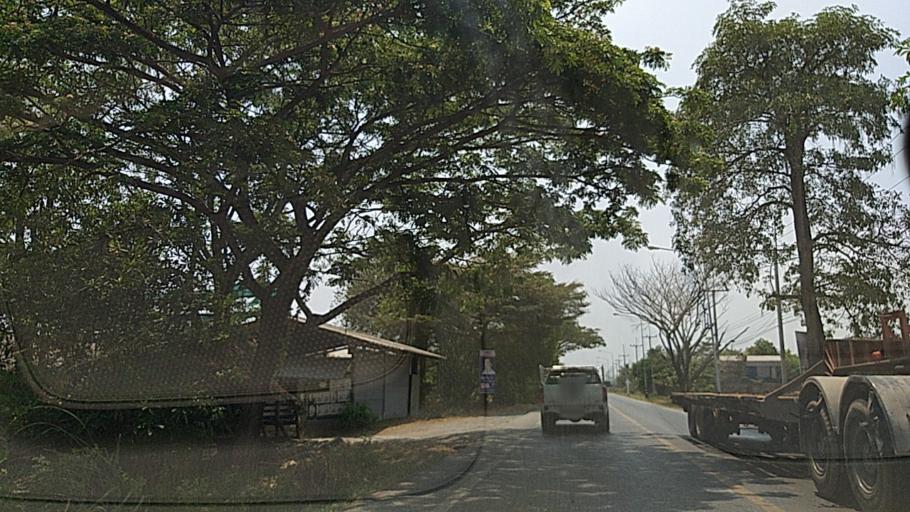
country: TH
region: Chachoengsao
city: Bang Nam Priao
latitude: 13.8674
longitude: 100.9668
